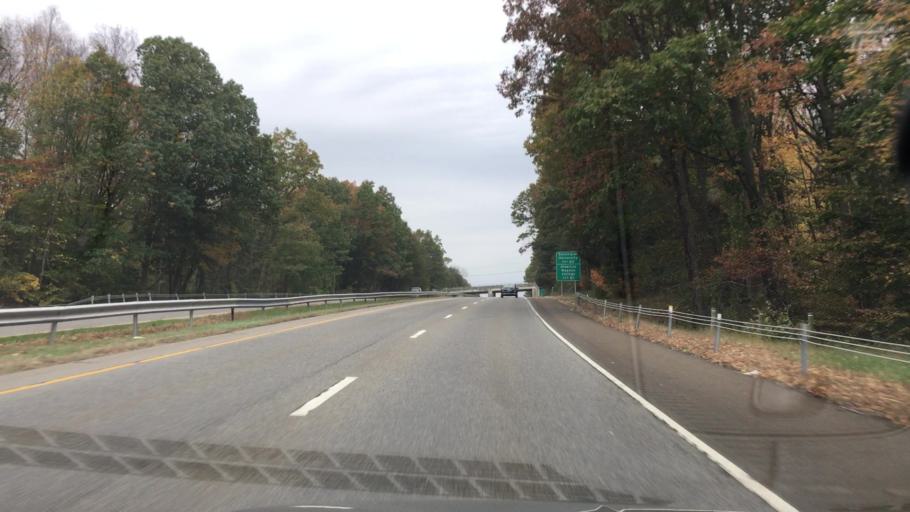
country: US
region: Connecticut
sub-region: New Haven County
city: Hamden
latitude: 41.3866
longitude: -72.8866
